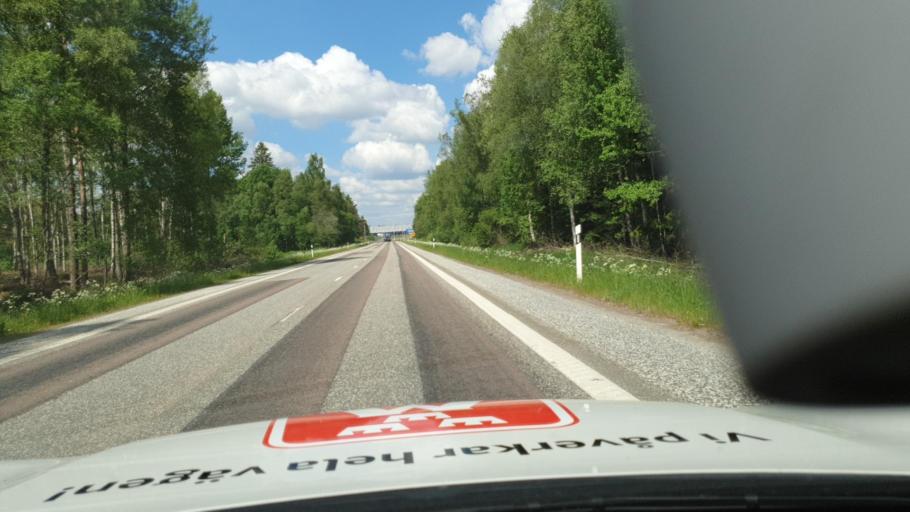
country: SE
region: Joenkoeping
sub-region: Jonkopings Kommun
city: Odensjo
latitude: 57.6431
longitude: 14.2007
